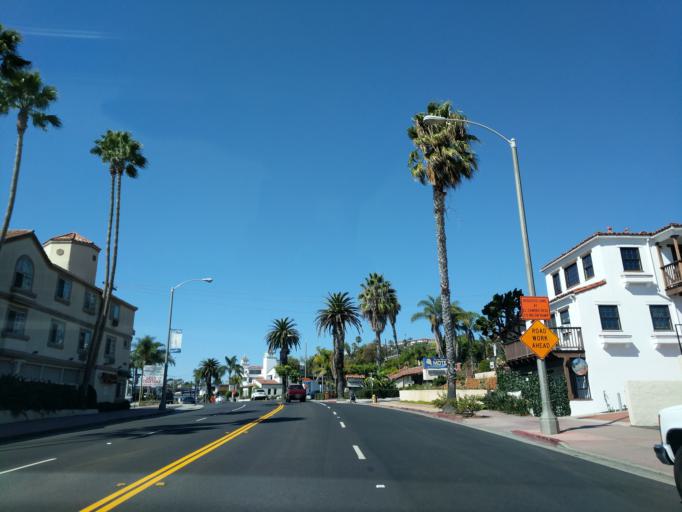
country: US
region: California
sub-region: Orange County
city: San Clemente
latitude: 33.4168
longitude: -117.6019
